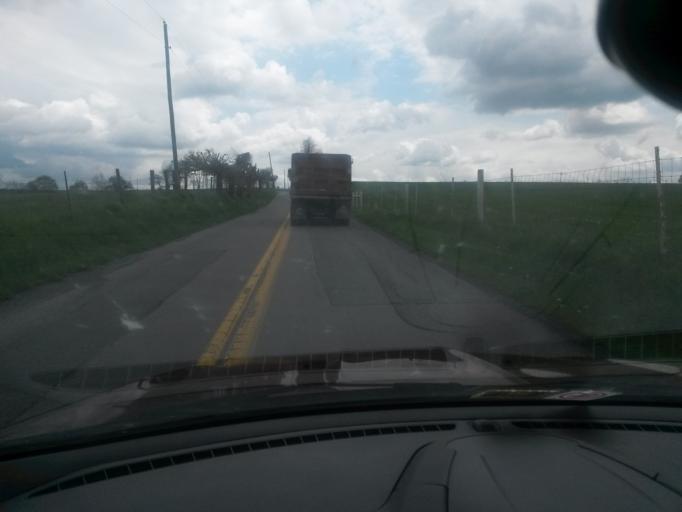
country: US
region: West Virginia
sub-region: Greenbrier County
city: Lewisburg
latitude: 37.8965
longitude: -80.4121
